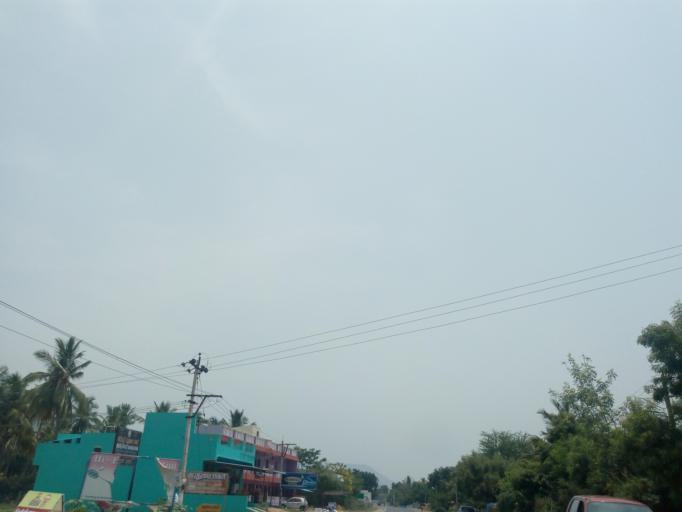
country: IN
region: Tamil Nadu
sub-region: Vellore
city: Vellore
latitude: 12.8711
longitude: 79.0961
